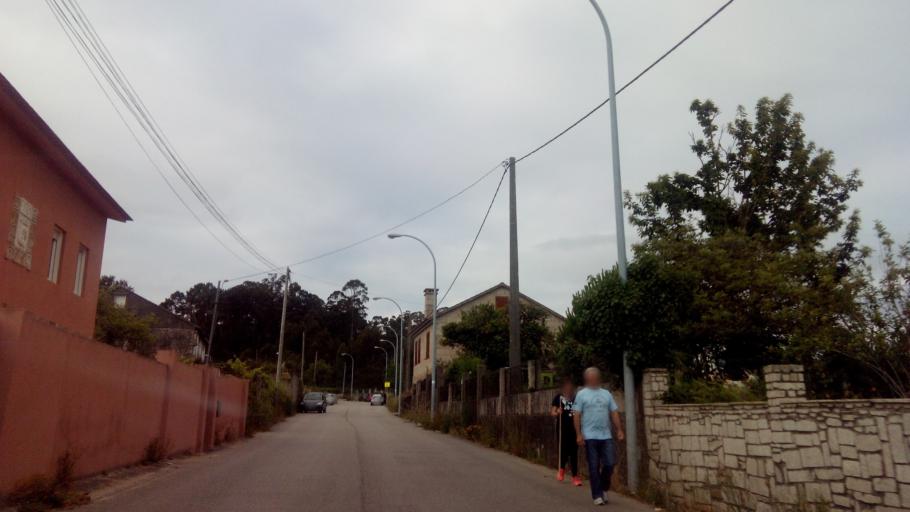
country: ES
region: Galicia
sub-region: Provincia de Pontevedra
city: Nigran
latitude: 42.1176
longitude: -8.8012
